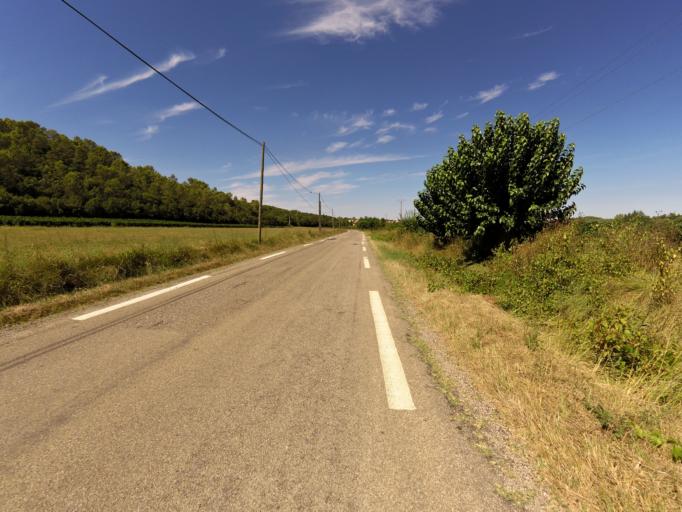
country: FR
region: Languedoc-Roussillon
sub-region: Departement du Gard
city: Quissac
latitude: 43.8652
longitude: 4.0400
